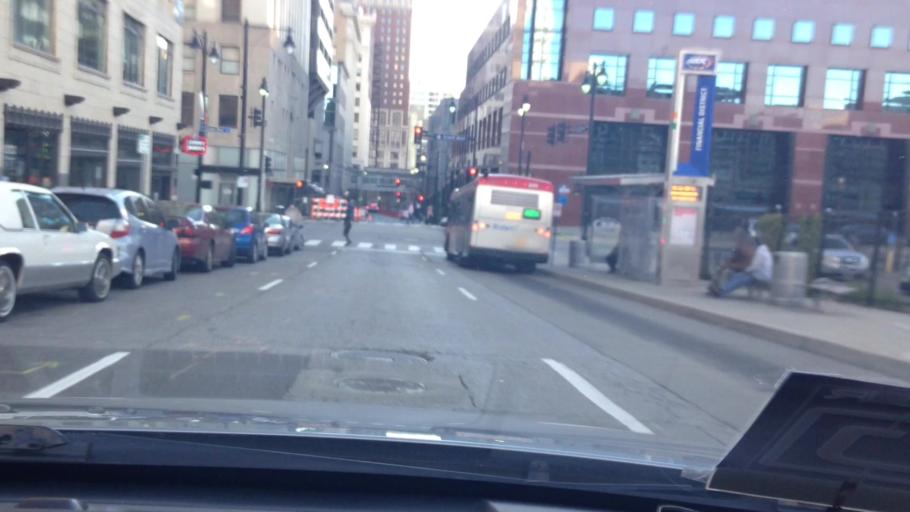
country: US
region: Missouri
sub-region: Jackson County
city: Kansas City
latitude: 39.1011
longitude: -94.5802
